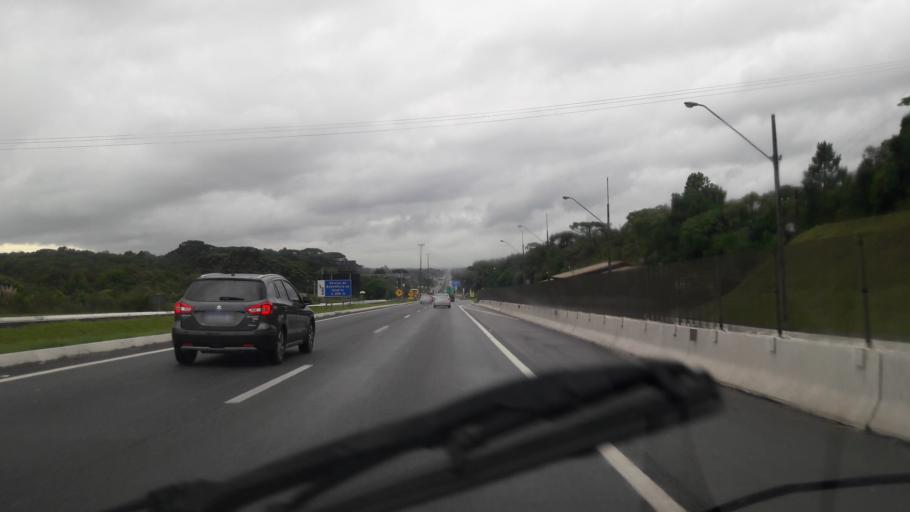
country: BR
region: Parana
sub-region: Piraquara
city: Piraquara
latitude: -25.5508
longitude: -49.0395
